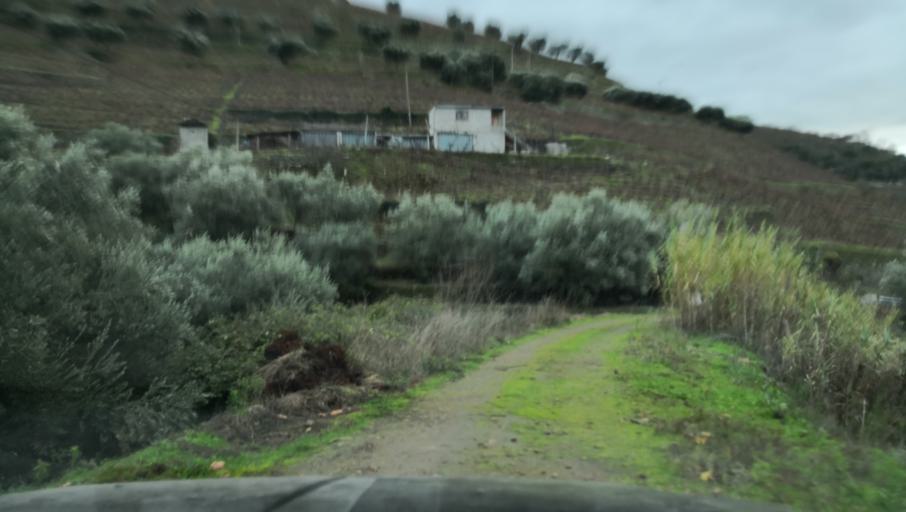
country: PT
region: Vila Real
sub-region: Peso da Regua
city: Peso da Regua
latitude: 41.1893
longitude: -7.7556
